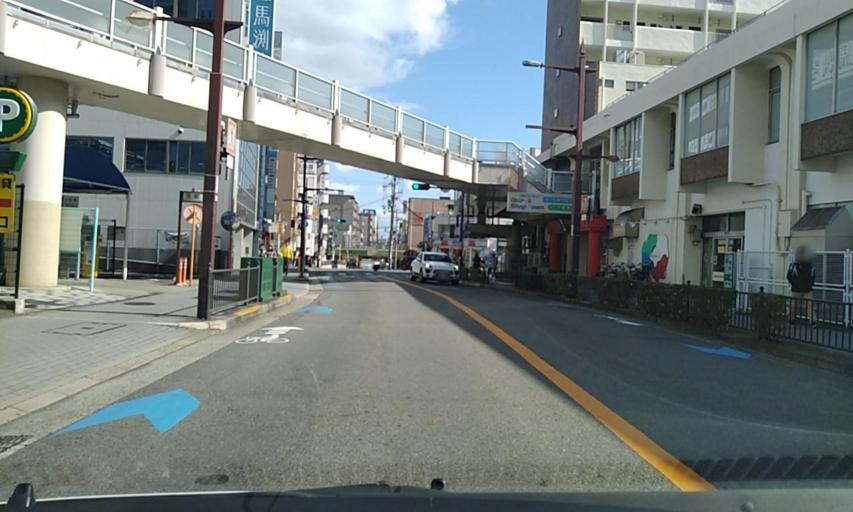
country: JP
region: Osaka
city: Ibaraki
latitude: 34.8169
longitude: 135.5617
